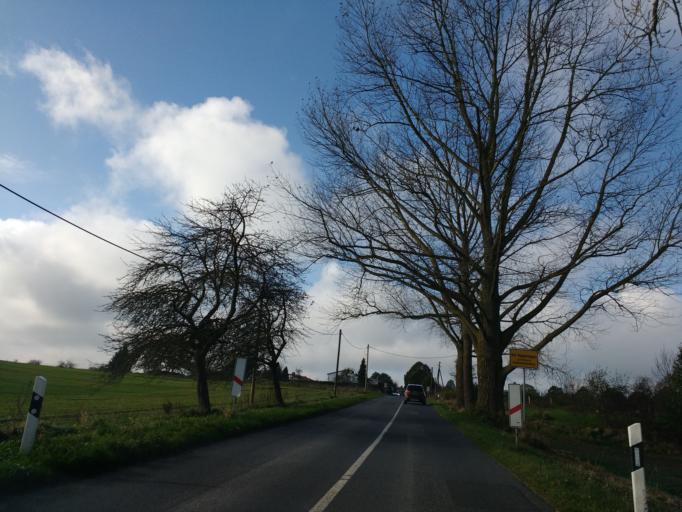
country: DE
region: Mecklenburg-Vorpommern
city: Klutz
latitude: 53.9339
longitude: 11.1248
